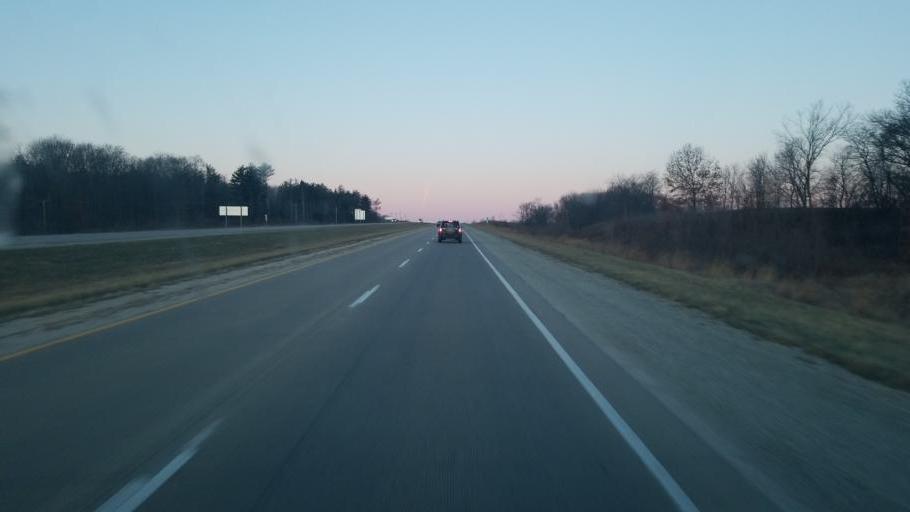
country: US
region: Iowa
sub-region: Henry County
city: Mount Pleasant
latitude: 40.9730
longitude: -91.6523
